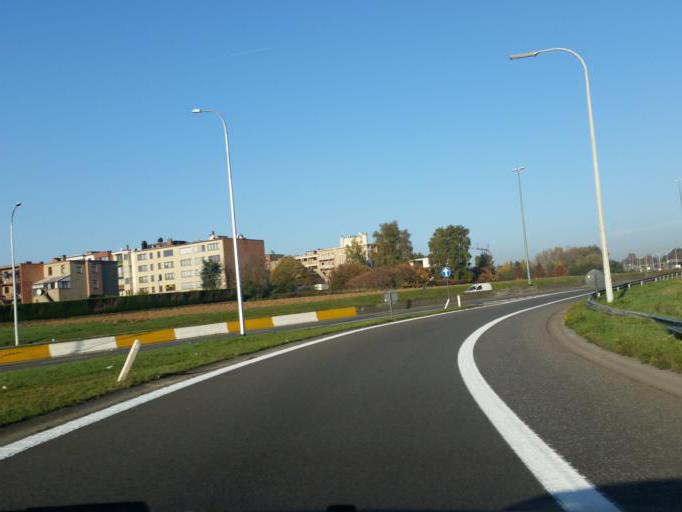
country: BE
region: Flanders
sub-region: Provincie Vlaams-Brabant
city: Wemmel
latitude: 50.8842
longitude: 4.2826
